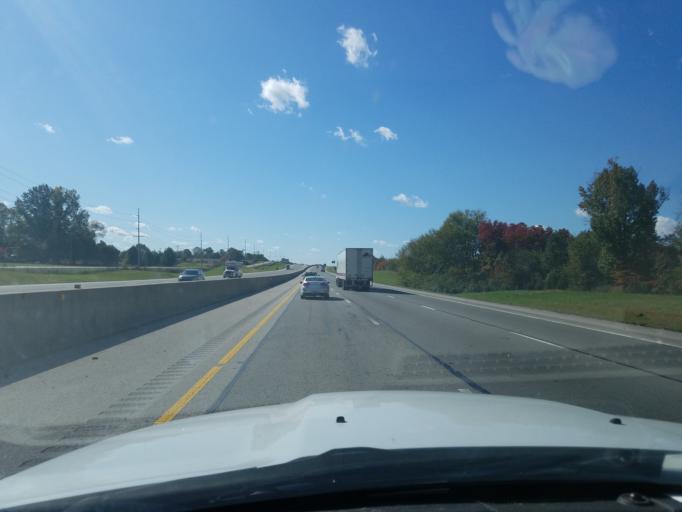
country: US
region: Kentucky
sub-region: Warren County
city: Bowling Green
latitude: 36.9704
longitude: -86.3949
